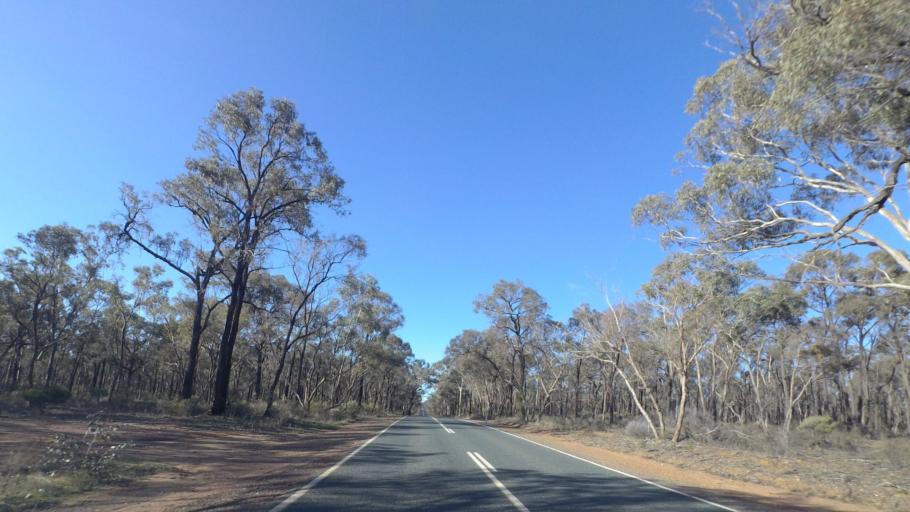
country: AU
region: Victoria
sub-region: Greater Bendigo
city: Epsom
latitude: -36.6690
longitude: 144.4237
